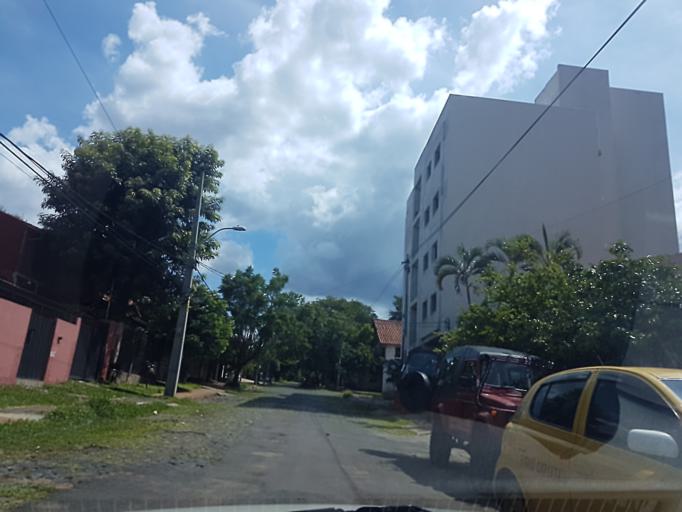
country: PY
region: Asuncion
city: Asuncion
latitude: -25.2734
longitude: -57.5735
